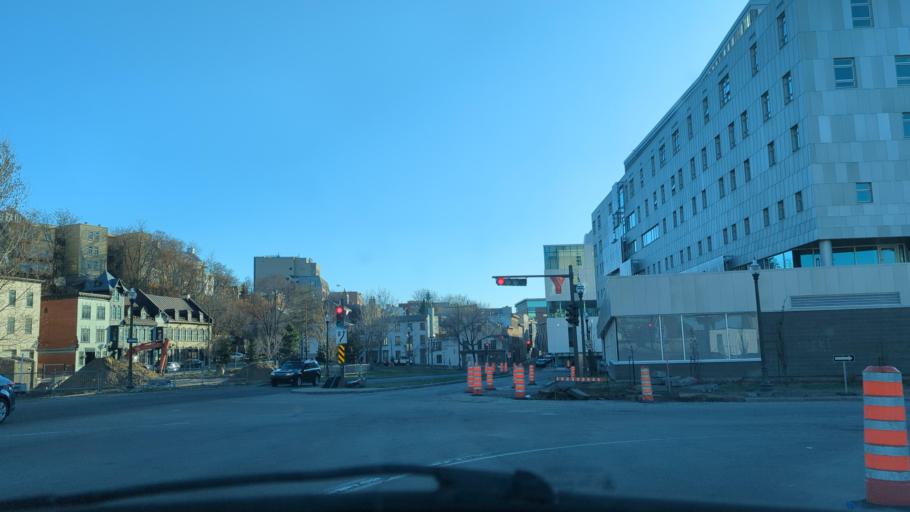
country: CA
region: Quebec
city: Quebec
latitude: 46.8143
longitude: -71.2181
